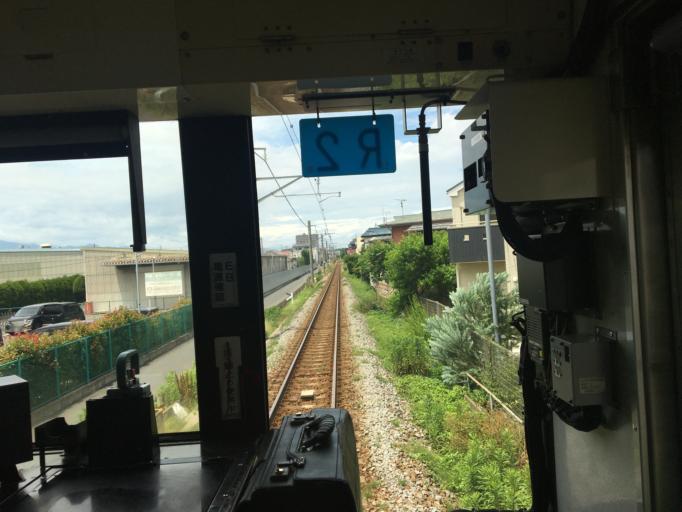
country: JP
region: Kanagawa
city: Chigasaki
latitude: 35.3427
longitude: 139.4057
